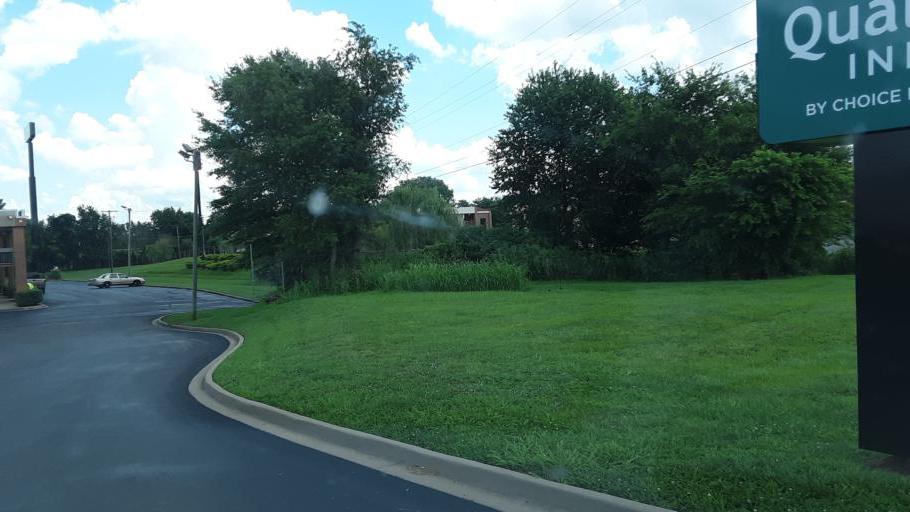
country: US
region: Tennessee
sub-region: Montgomery County
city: Clarksville
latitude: 36.5963
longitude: -87.2842
